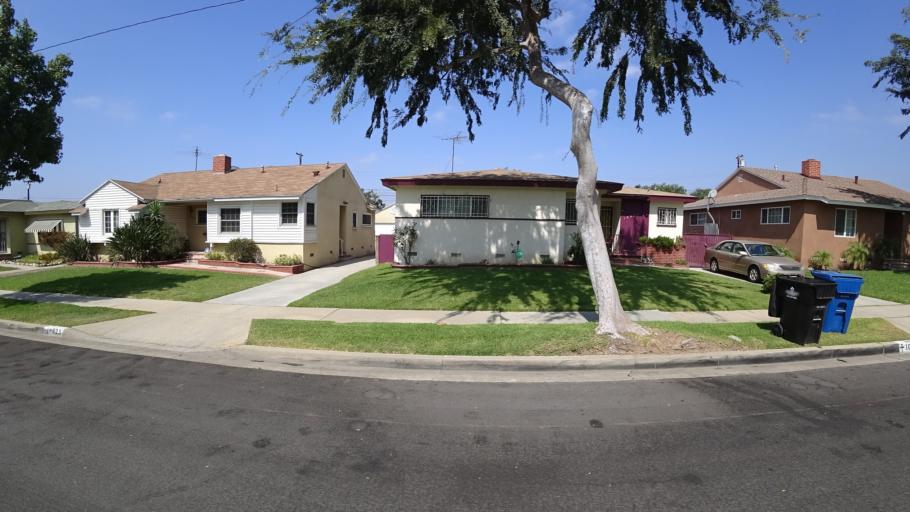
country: US
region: California
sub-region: Los Angeles County
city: Westmont
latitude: 33.9366
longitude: -118.3236
